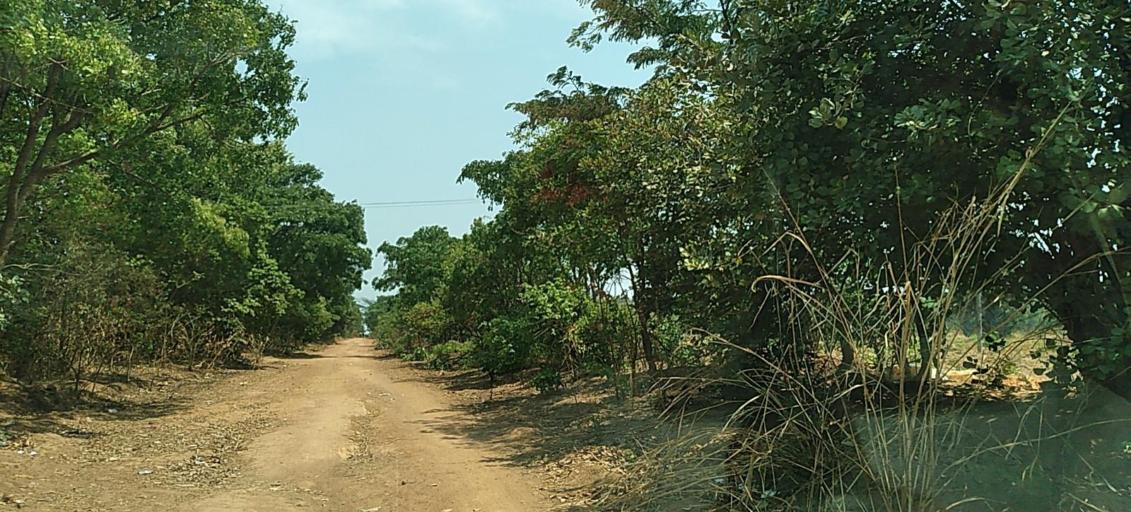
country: ZM
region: Copperbelt
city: Ndola
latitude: -13.0576
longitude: 28.7379
